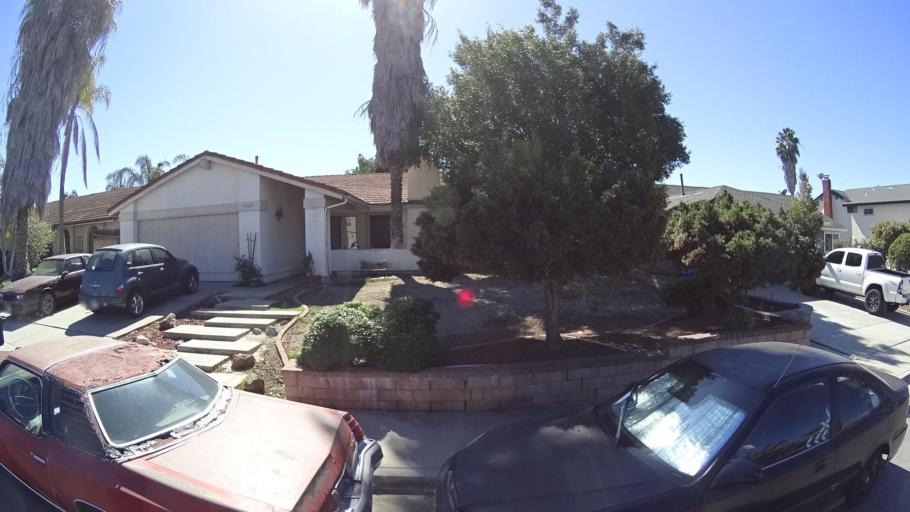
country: US
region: California
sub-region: San Diego County
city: La Presa
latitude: 32.6988
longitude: -117.0017
